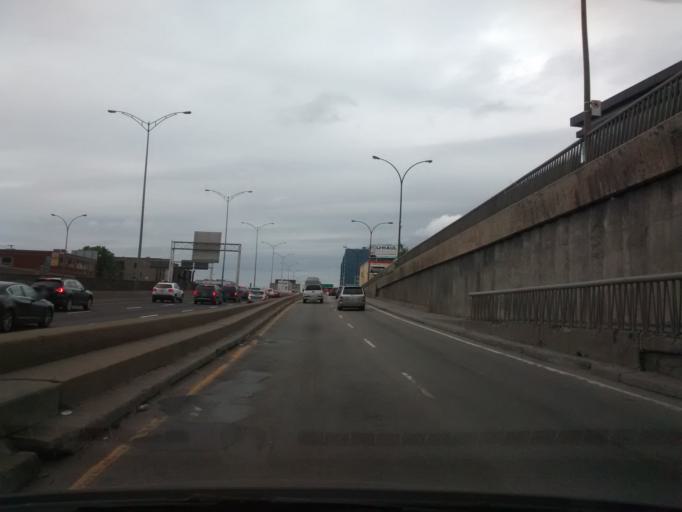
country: CA
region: Quebec
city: Mont-Royal
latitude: 45.5352
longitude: -73.6455
